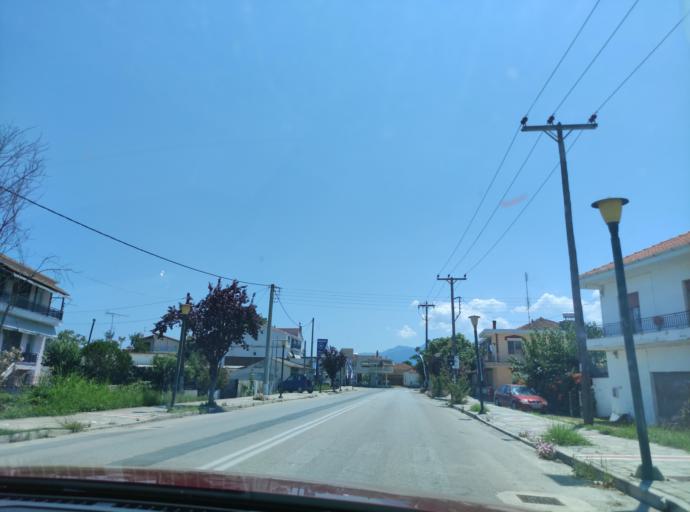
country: GR
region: East Macedonia and Thrace
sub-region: Nomos Kavalas
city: Keramoti
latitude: 40.8606
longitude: 24.7057
